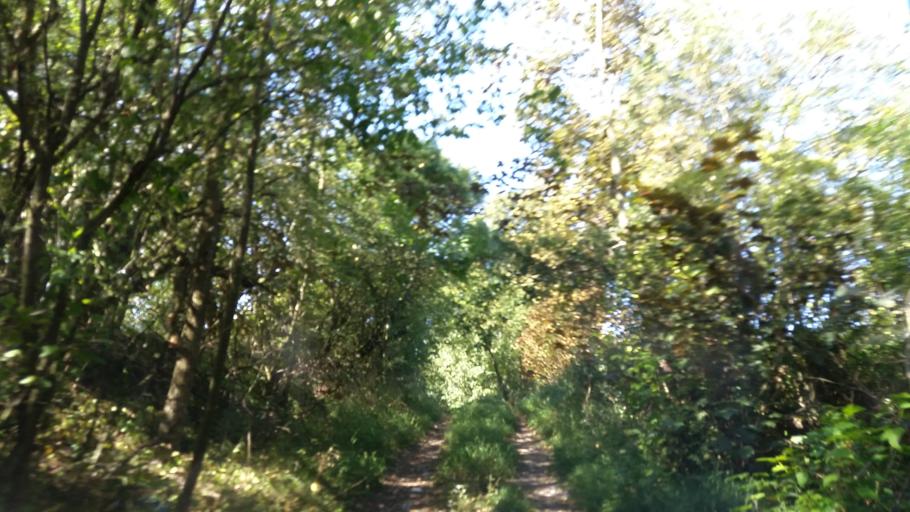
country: PL
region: West Pomeranian Voivodeship
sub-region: Powiat choszczenski
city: Krzecin
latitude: 53.1253
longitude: 15.5020
